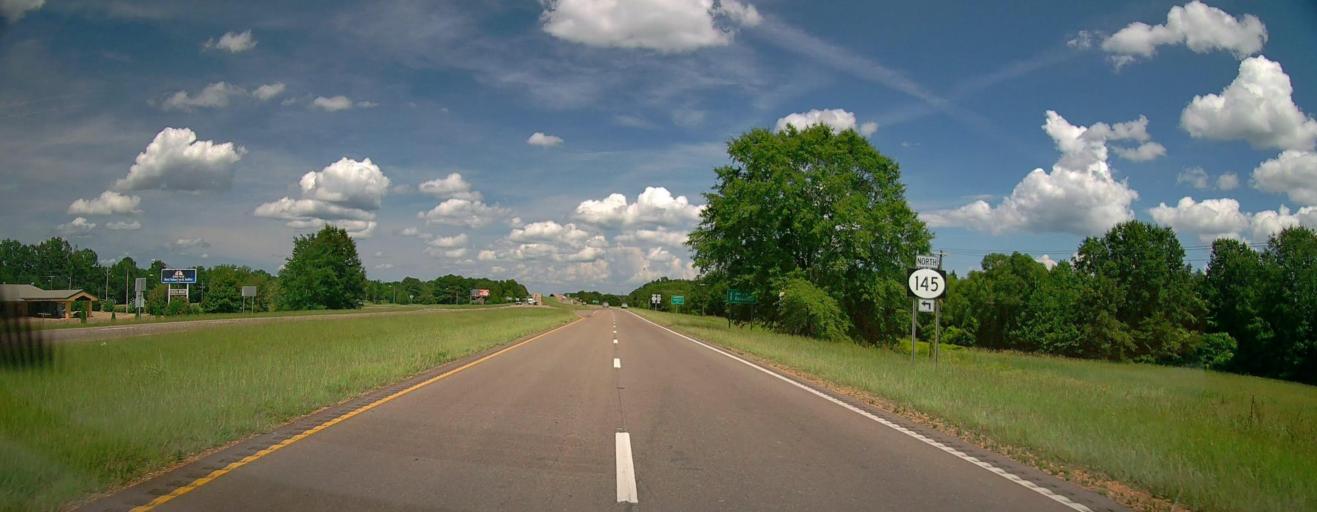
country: US
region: Mississippi
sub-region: Monroe County
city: Aberdeen
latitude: 33.8160
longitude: -88.5308
